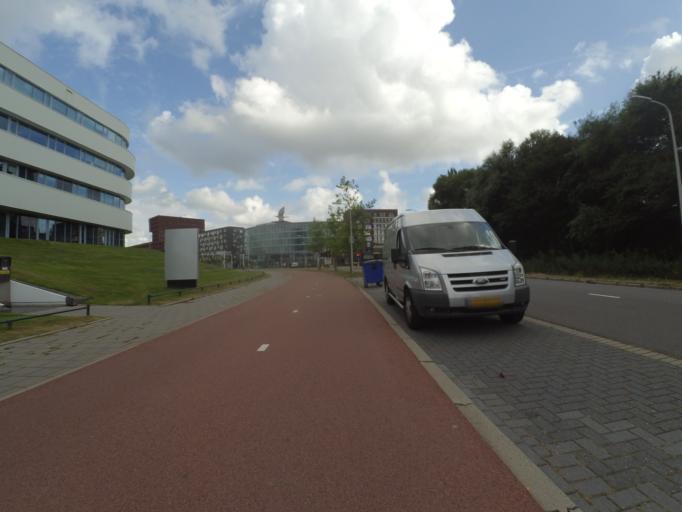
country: NL
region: South Holland
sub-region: Gemeente Den Haag
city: Ypenburg
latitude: 52.0555
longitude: 4.3871
